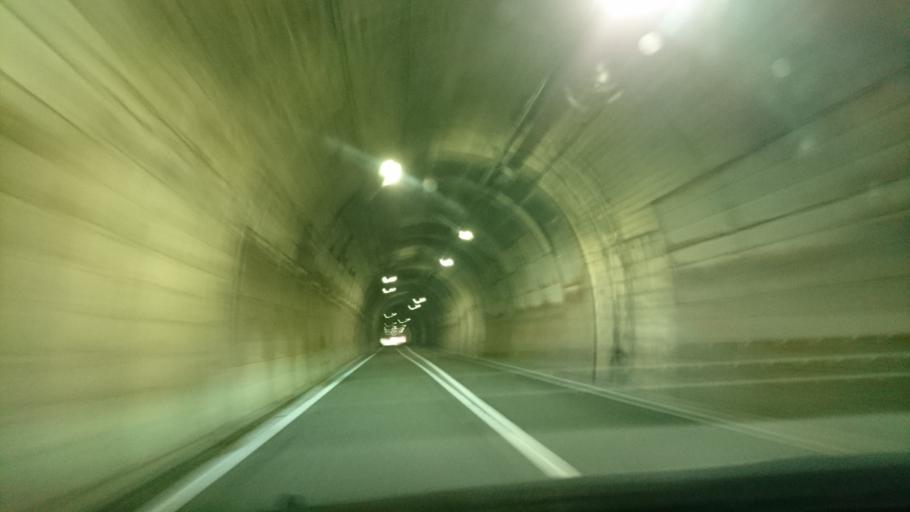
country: JP
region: Iwate
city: Kitakami
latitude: 39.3017
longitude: 140.8800
